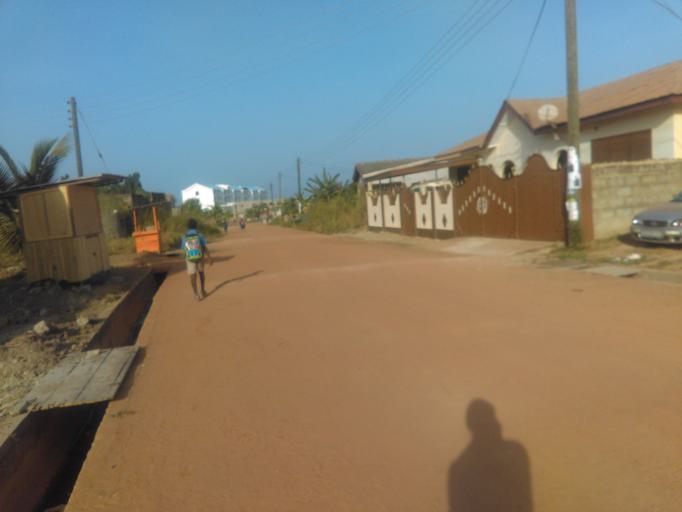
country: GH
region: Central
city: Cape Coast
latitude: 5.1095
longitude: -1.2975
